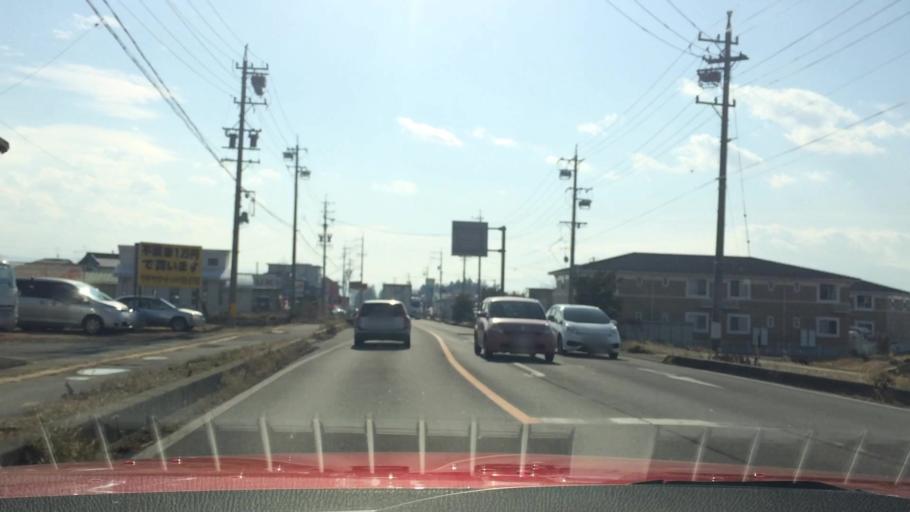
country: JP
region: Nagano
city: Komoro
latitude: 36.3116
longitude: 138.4949
